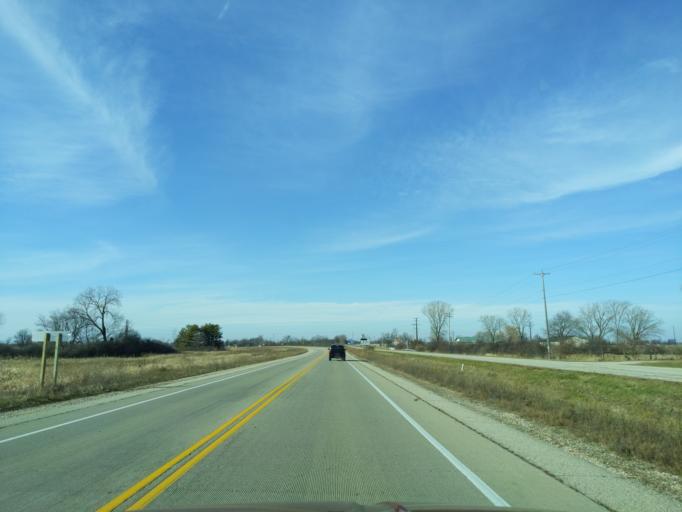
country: US
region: Wisconsin
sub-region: Walworth County
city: Whitewater
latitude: 42.8162
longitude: -88.6918
